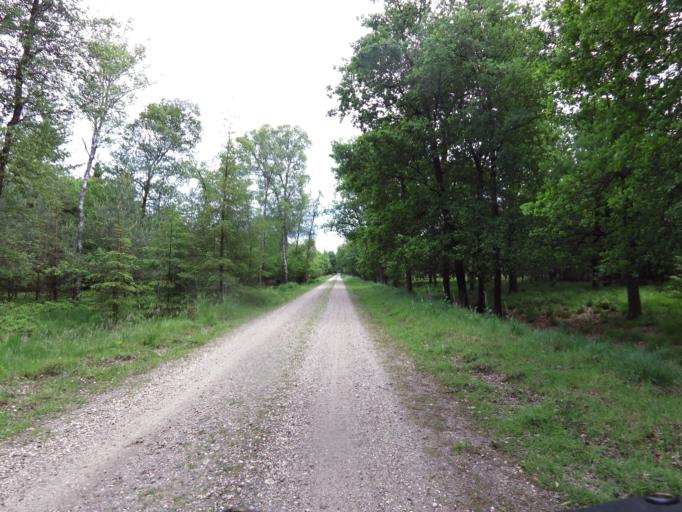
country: NL
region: Gelderland
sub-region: Gemeente Apeldoorn
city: Uddel
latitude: 52.2678
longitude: 5.8271
